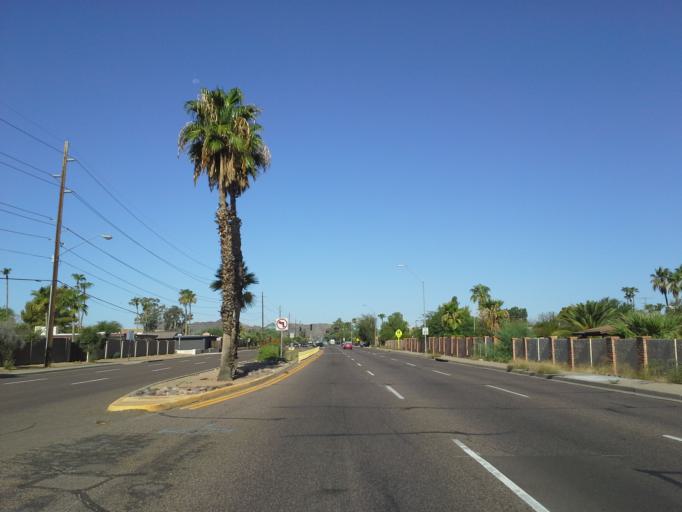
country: US
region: Arizona
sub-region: Maricopa County
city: Paradise Valley
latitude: 33.5828
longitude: -111.9931
